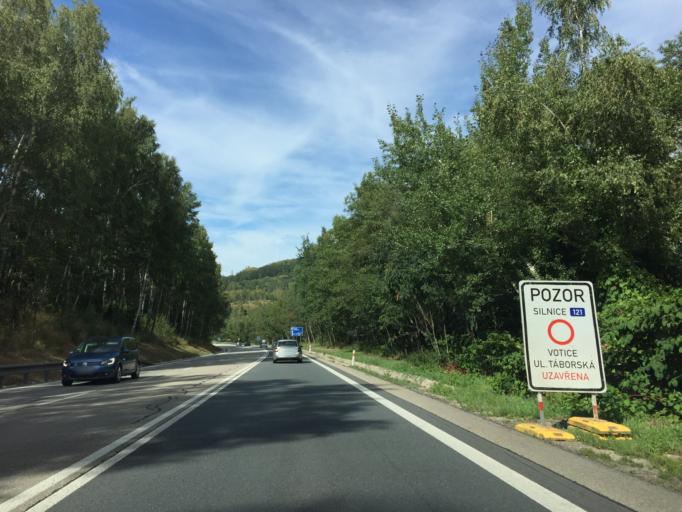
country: CZ
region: Central Bohemia
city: Votice
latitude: 49.6337
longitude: 14.6513
